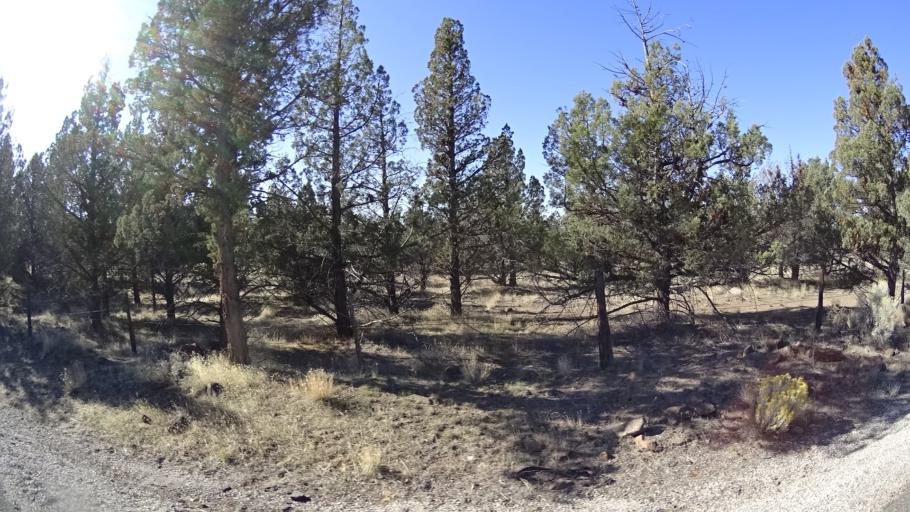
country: US
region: California
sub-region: Siskiyou County
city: Weed
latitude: 41.6074
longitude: -122.3095
